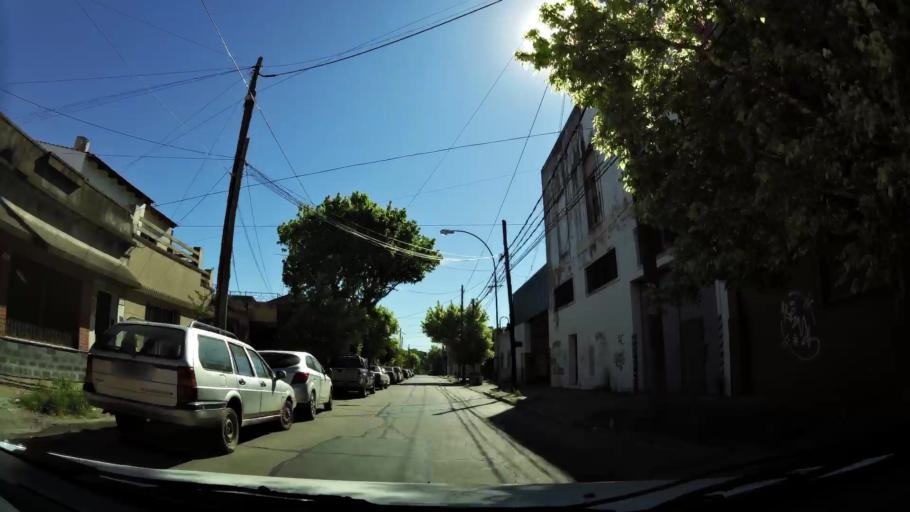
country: AR
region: Buenos Aires
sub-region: Partido de General San Martin
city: General San Martin
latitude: -34.5447
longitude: -58.5125
